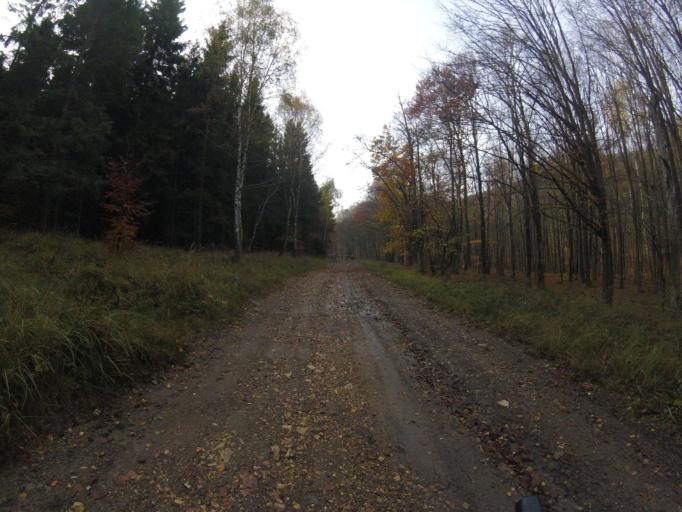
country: HU
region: Borsod-Abauj-Zemplen
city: Gonc
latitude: 48.4278
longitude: 21.3726
